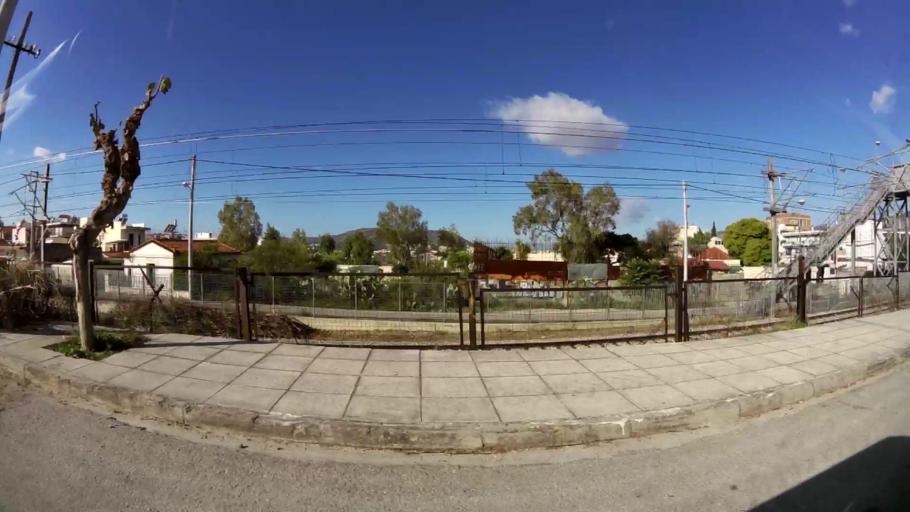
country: GR
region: Attica
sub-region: Nomarchia Anatolikis Attikis
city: Acharnes
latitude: 38.0743
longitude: 23.7356
